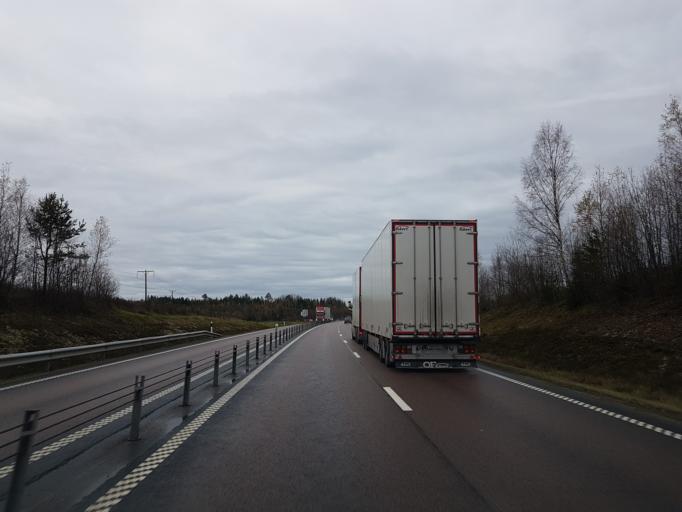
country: SE
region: Gaevleborg
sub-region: Hudiksvalls Kommun
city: Hudiksvall
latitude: 61.7596
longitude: 17.0916
